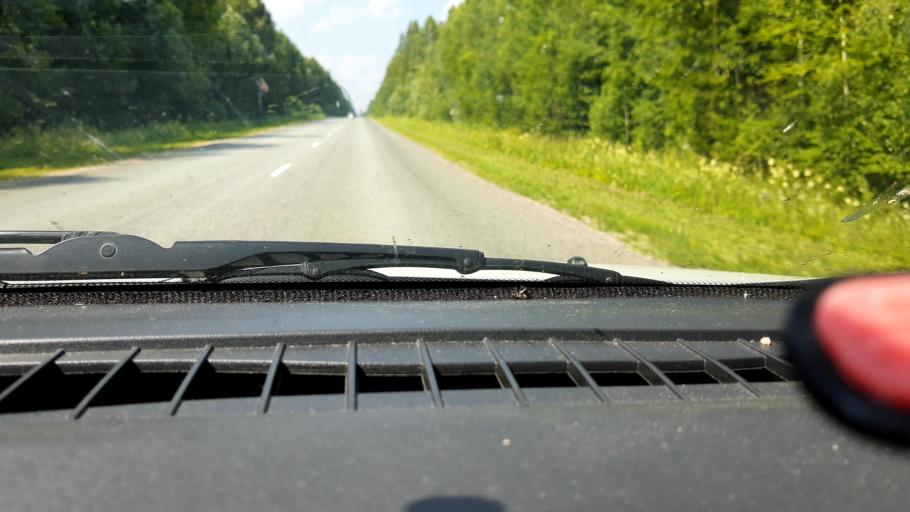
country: RU
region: Nizjnij Novgorod
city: Sharanga
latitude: 57.2316
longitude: 46.4931
